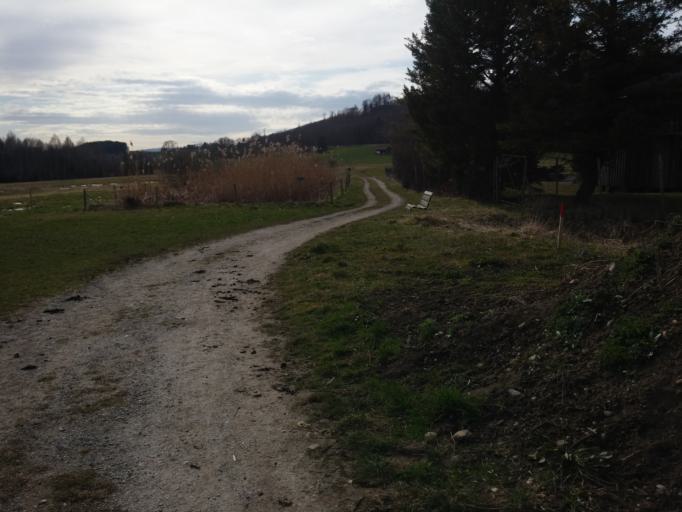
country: DE
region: Bavaria
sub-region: Swabia
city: Wildpoldsried
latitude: 47.7666
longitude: 10.3951
